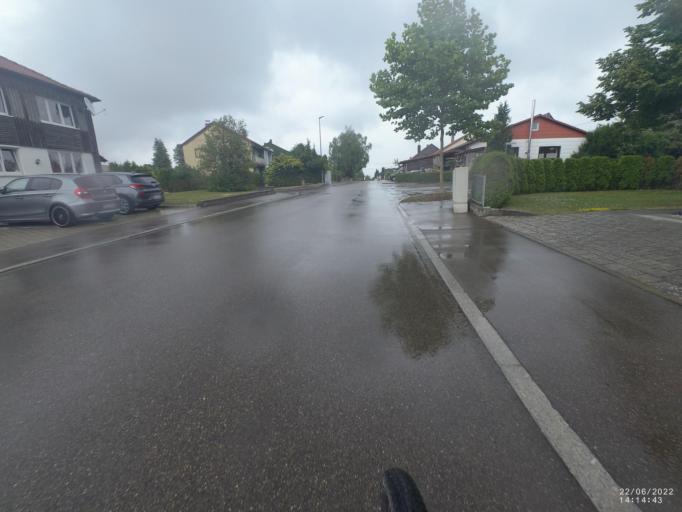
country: DE
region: Baden-Wuerttemberg
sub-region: Regierungsbezirk Stuttgart
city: Gerstetten
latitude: 48.6242
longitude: 10.0323
